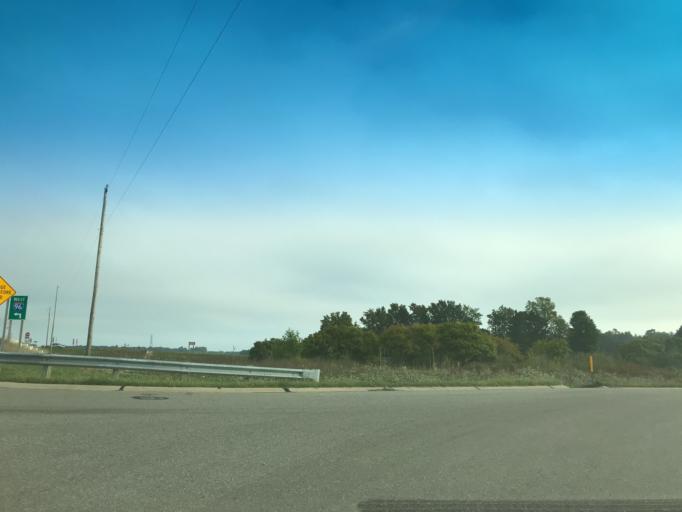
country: US
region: Michigan
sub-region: Eaton County
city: Grand Ledge
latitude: 42.7992
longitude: -84.7393
